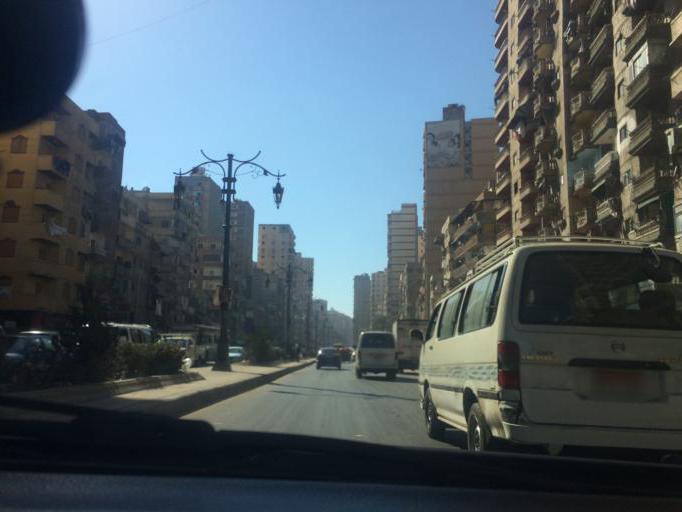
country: EG
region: Alexandria
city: Alexandria
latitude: 31.2634
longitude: 30.0069
